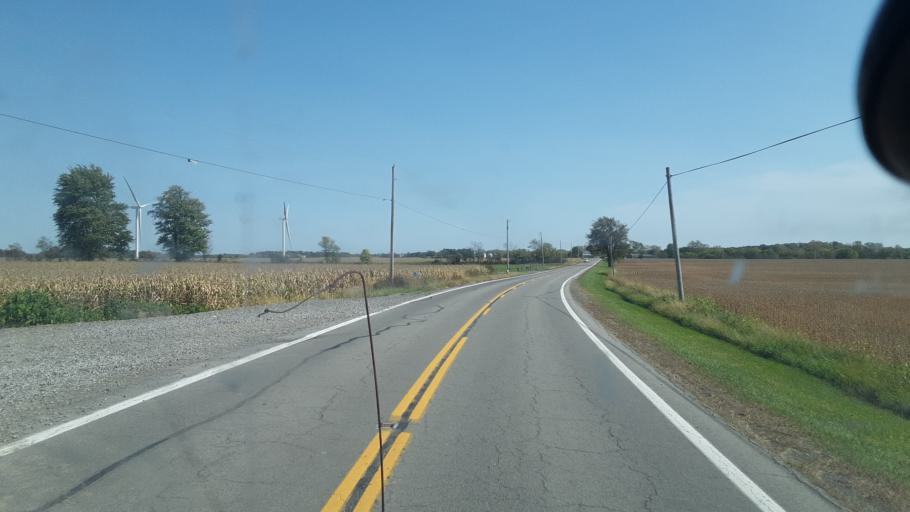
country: US
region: Ohio
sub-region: Logan County
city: Northwood
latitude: 40.5050
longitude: -83.7197
